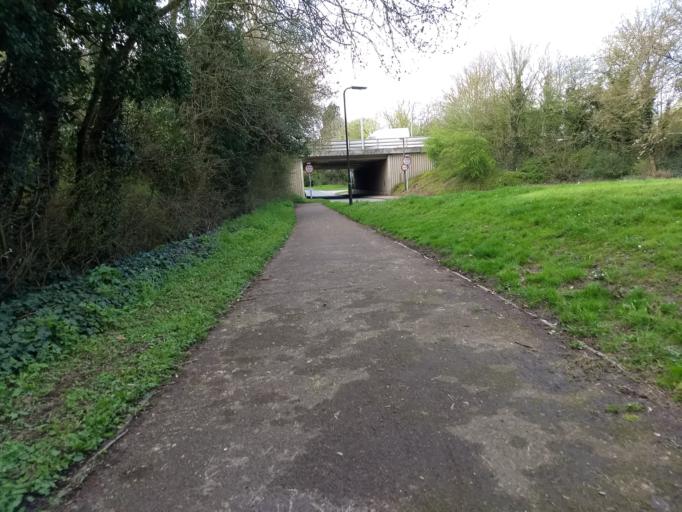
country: GB
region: England
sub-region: Milton Keynes
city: Simpson
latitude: 52.0251
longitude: -0.7207
